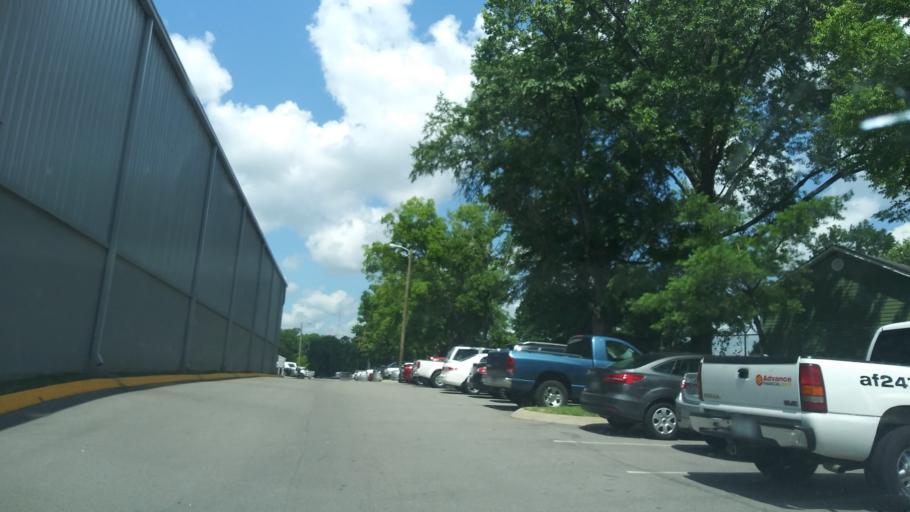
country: US
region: Tennessee
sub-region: Davidson County
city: Nashville
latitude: 36.1281
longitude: -86.7686
